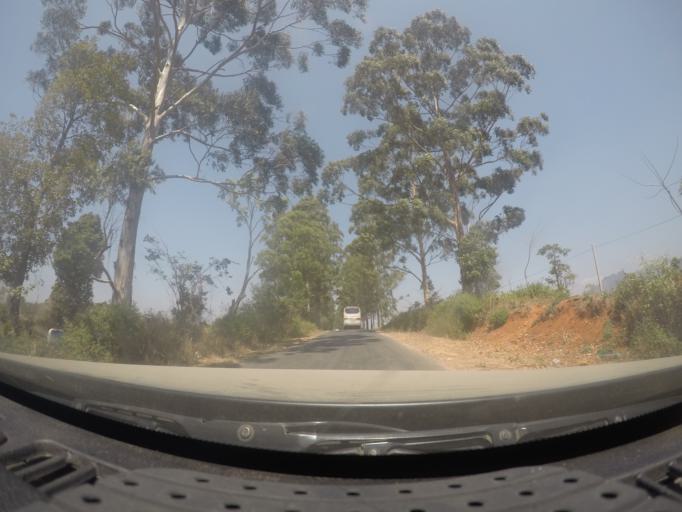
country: MM
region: Shan
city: Taunggyi
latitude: 20.9499
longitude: 96.5469
